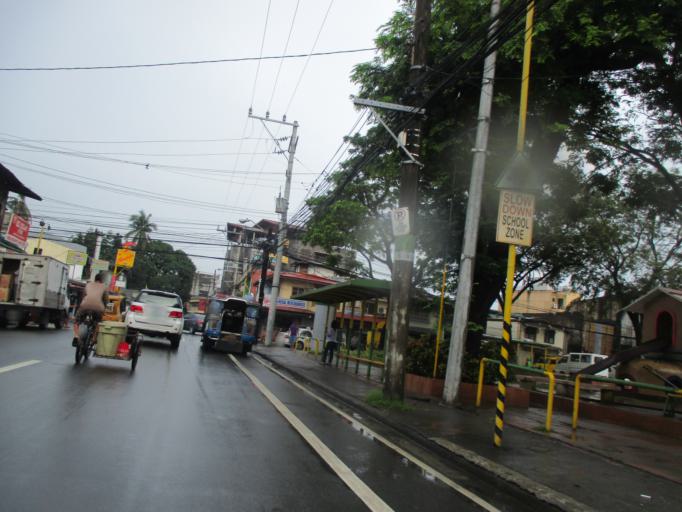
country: PH
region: Metro Manila
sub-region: Marikina
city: Calumpang
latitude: 14.6231
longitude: 121.0965
